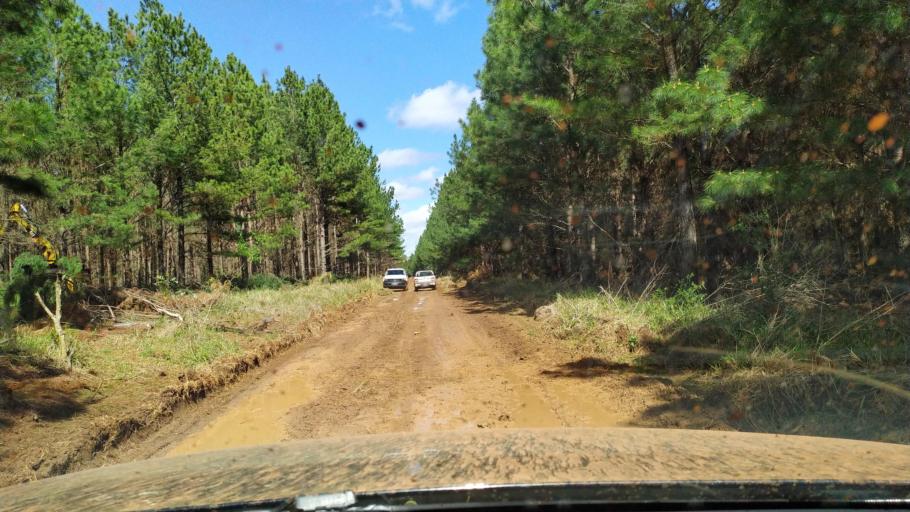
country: AR
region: Corrientes
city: Santo Tome
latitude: -28.4054
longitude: -56.0148
